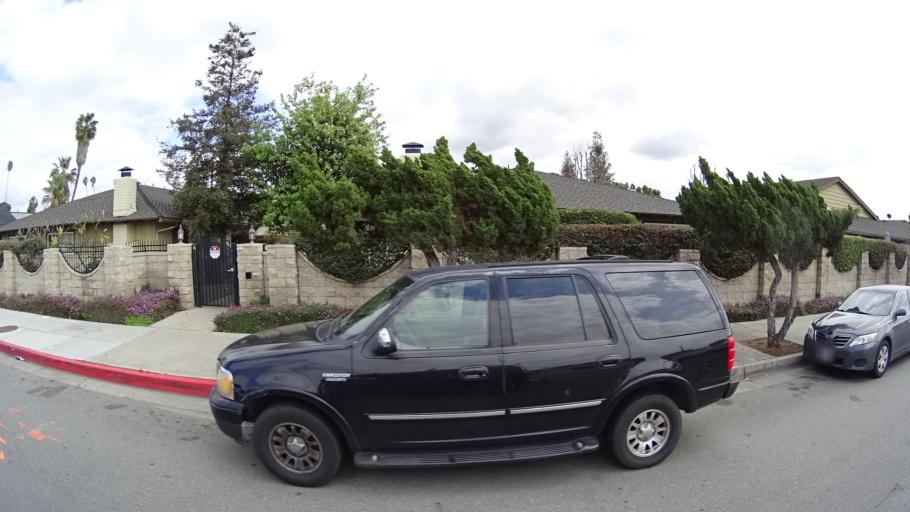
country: US
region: California
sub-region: Orange County
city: Stanton
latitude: 33.8310
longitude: -117.9759
